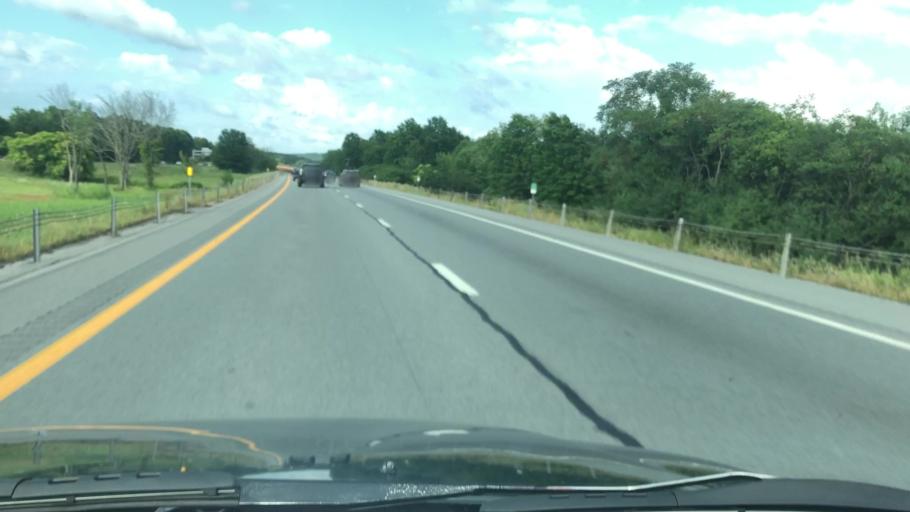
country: US
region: New York
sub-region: Orange County
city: Scotchtown
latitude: 41.4562
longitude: -74.3528
